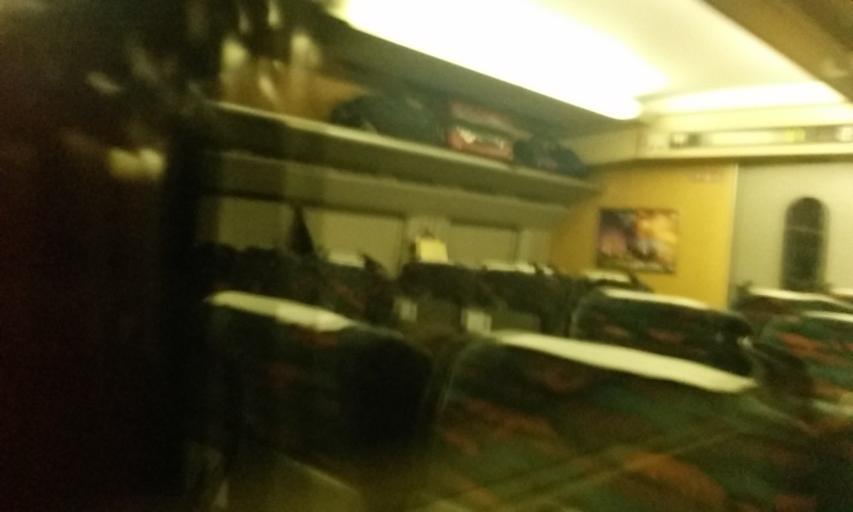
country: JP
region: Miyagi
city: Okawara
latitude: 38.0326
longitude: 140.6757
